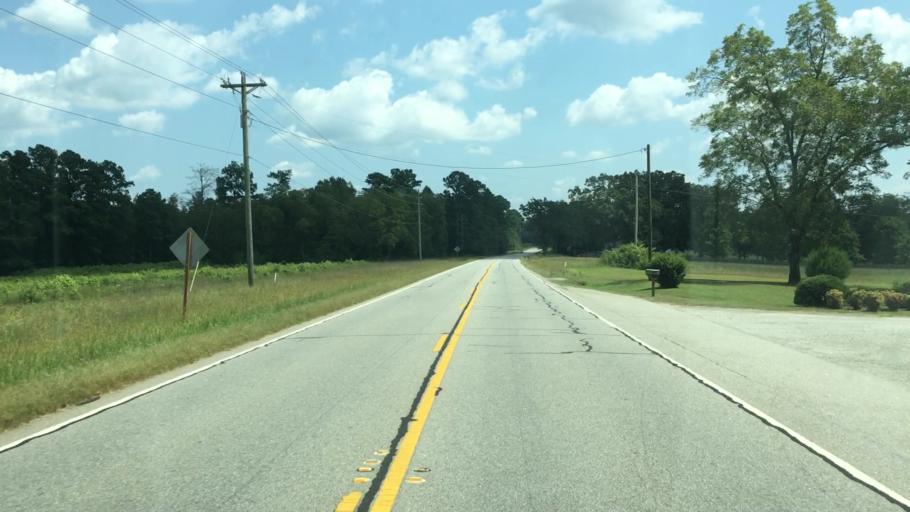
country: US
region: Georgia
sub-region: Oconee County
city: Bogart
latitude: 33.8936
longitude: -83.5664
